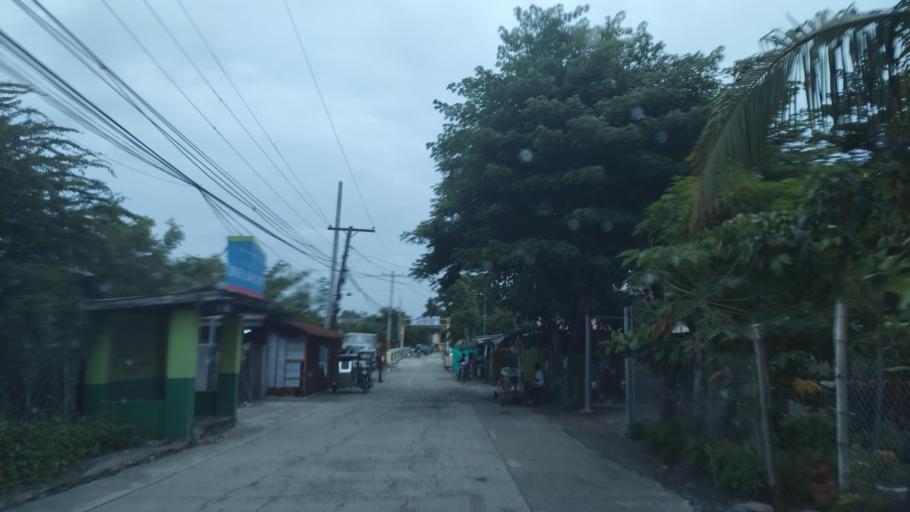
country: PH
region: Central Luzon
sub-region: Province of Nueva Ecija
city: San Anton
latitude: 15.3605
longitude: 120.9035
